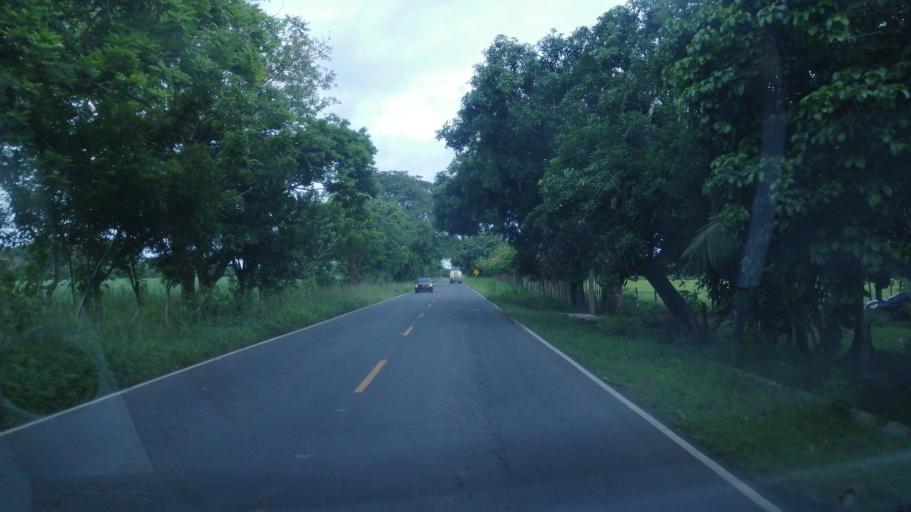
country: PA
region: Chiriqui
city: Alanje
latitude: 8.4102
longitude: -82.5160
